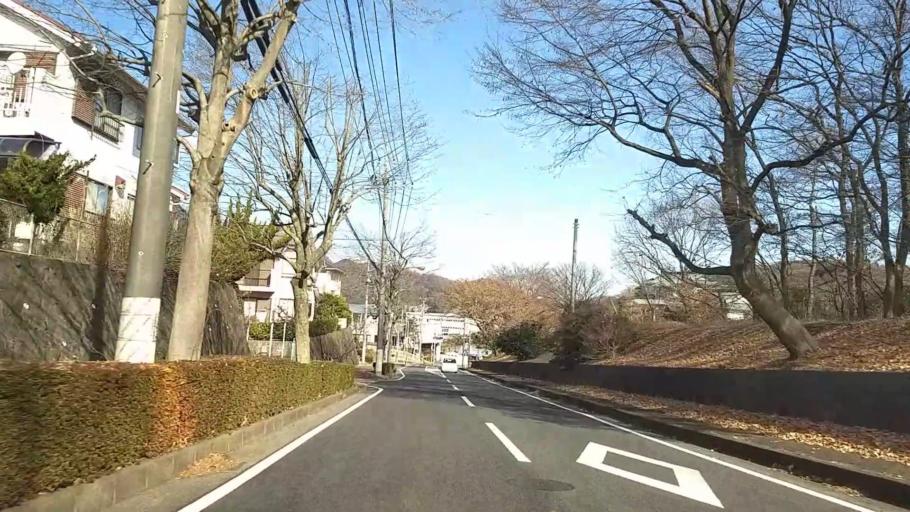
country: JP
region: Kanagawa
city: Hadano
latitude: 35.3551
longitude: 139.2330
